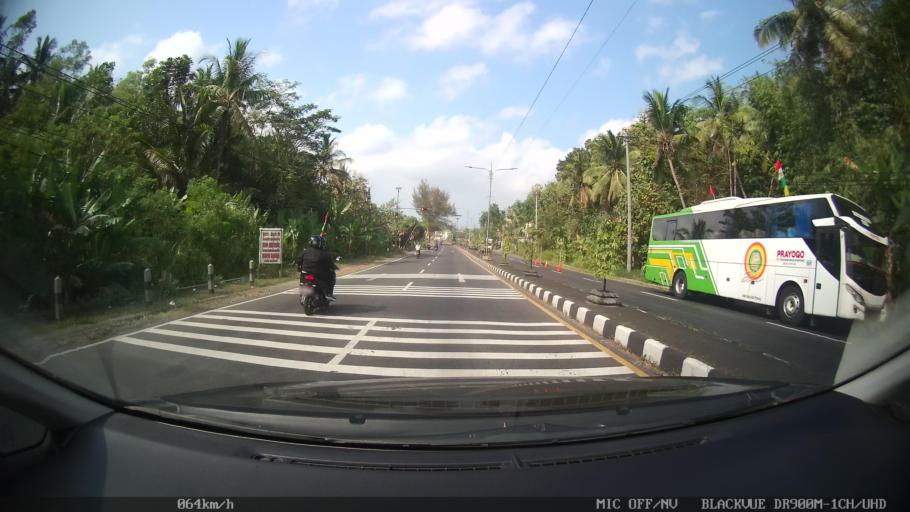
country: ID
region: Daerah Istimewa Yogyakarta
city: Srandakan
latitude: -7.8525
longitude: 110.2164
